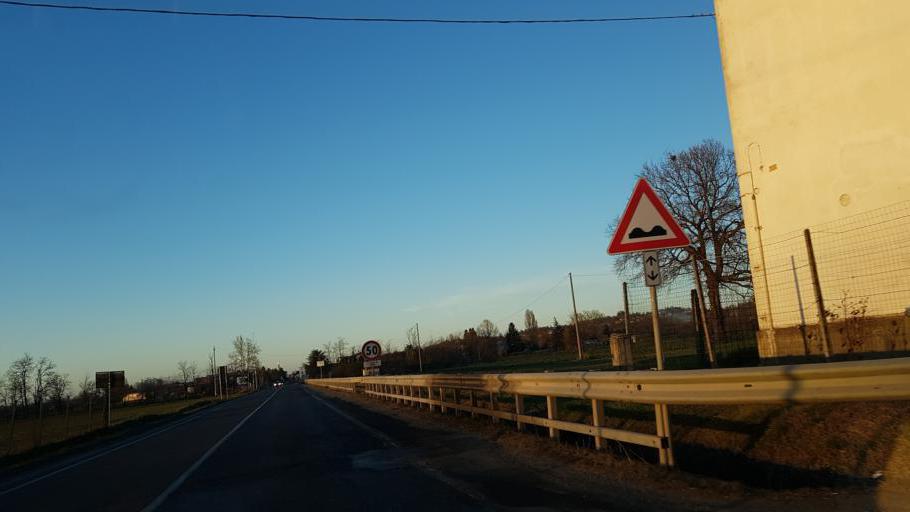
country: IT
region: Piedmont
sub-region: Provincia di Alessandria
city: Carbonara Scrivia
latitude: 44.8668
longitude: 8.8562
